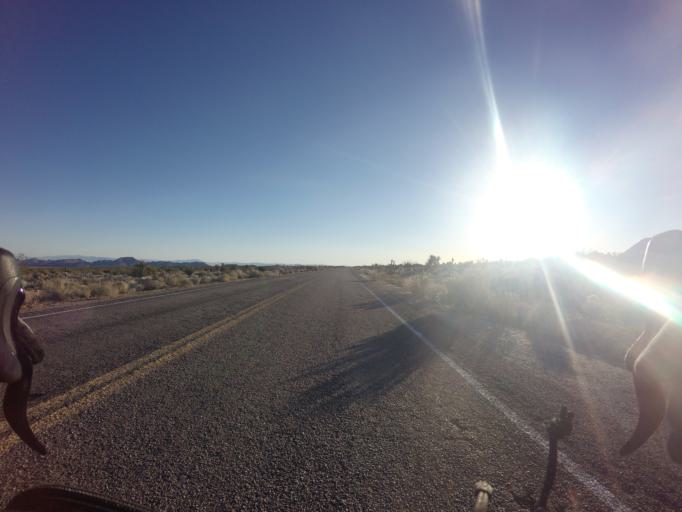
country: US
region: California
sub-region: San Bernardino County
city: Twentynine Palms
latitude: 34.7725
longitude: -115.6284
